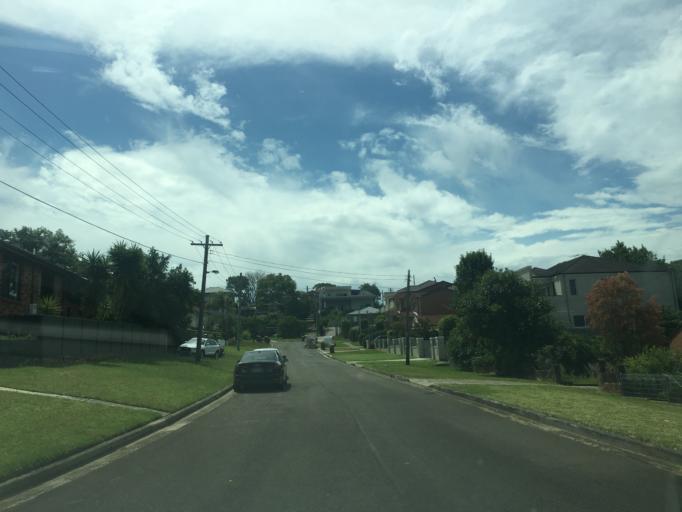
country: AU
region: New South Wales
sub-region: Ryde
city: North Ryde
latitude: -33.8044
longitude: 151.1081
